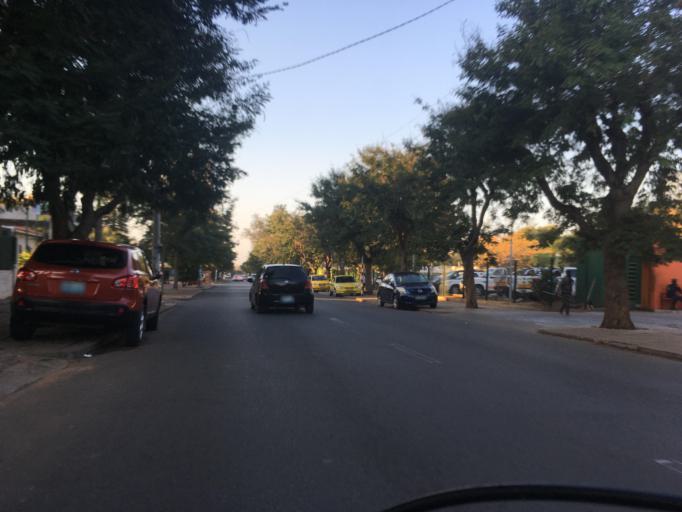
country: MZ
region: Maputo City
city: Maputo
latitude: -25.9685
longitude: 32.5932
